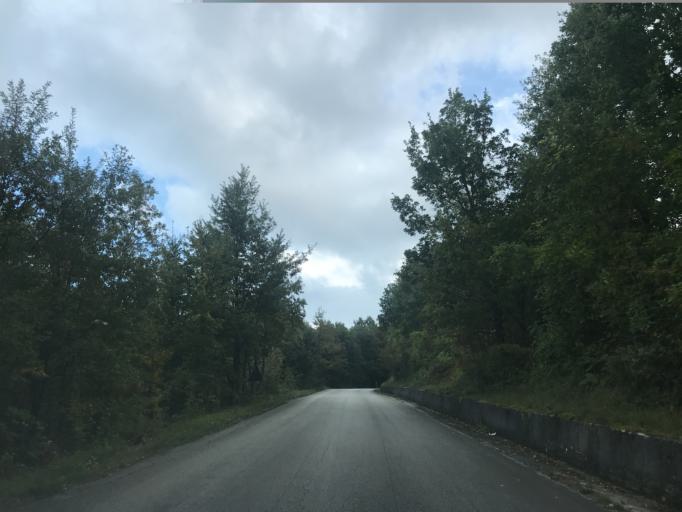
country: IT
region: Molise
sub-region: Provincia di Campobasso
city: Duronia
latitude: 41.6635
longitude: 14.4598
